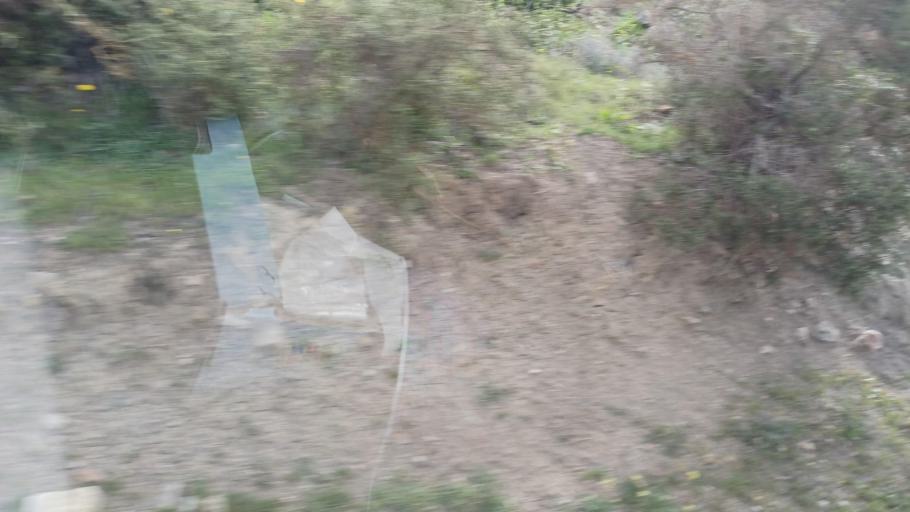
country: CY
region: Pafos
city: Pegeia
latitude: 34.9498
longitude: 32.3526
